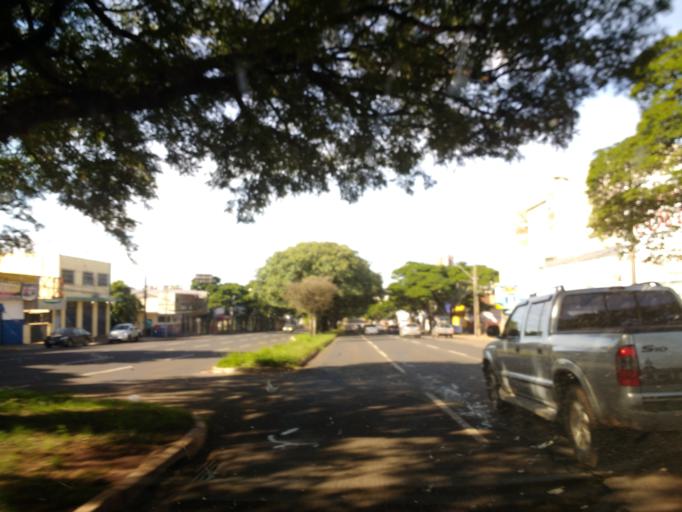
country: BR
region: Parana
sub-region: Maringa
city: Maringa
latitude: -23.4154
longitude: -51.9526
